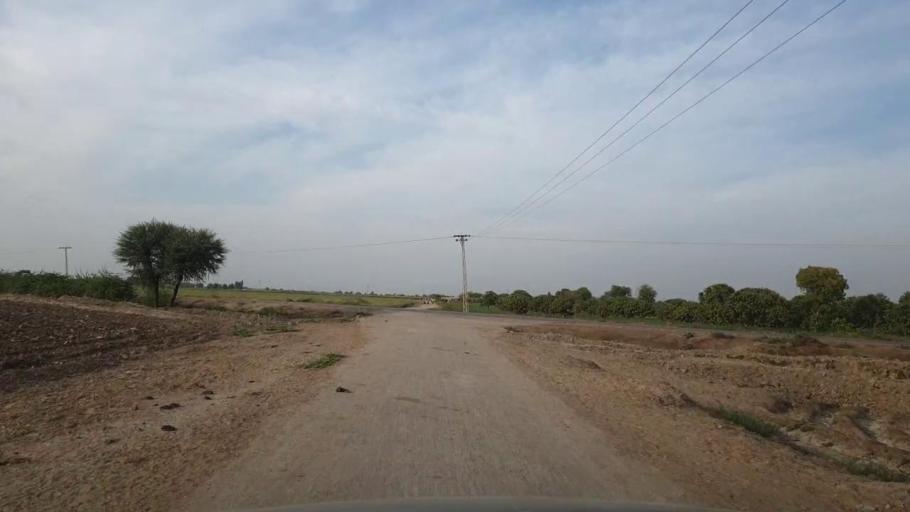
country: PK
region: Sindh
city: Kunri
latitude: 25.2016
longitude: 69.5199
